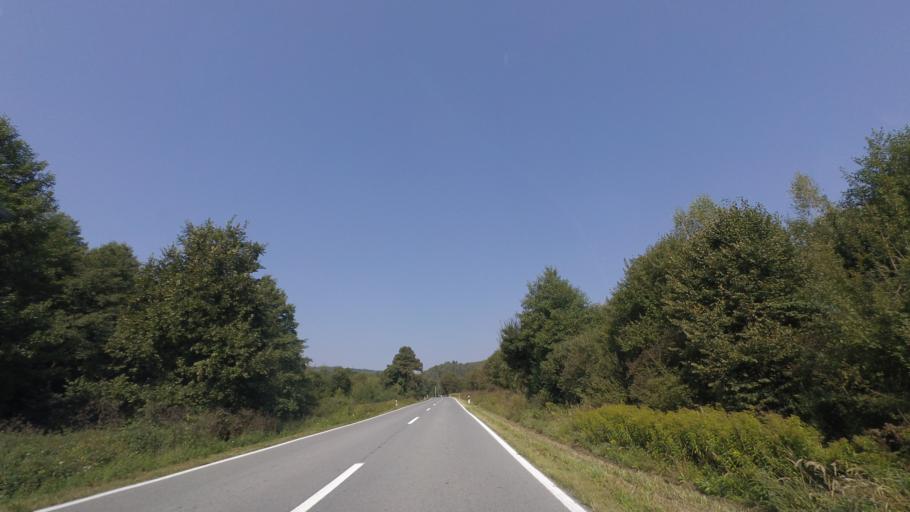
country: HR
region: Pozesko-Slavonska
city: Velika
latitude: 45.4407
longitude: 17.4853
